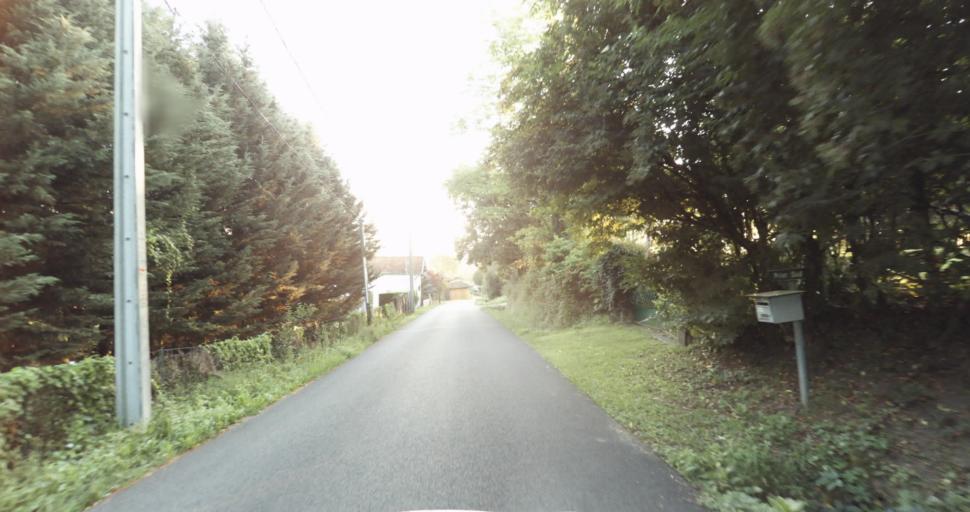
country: FR
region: Aquitaine
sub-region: Departement de la Gironde
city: Bazas
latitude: 44.4306
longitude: -0.2027
